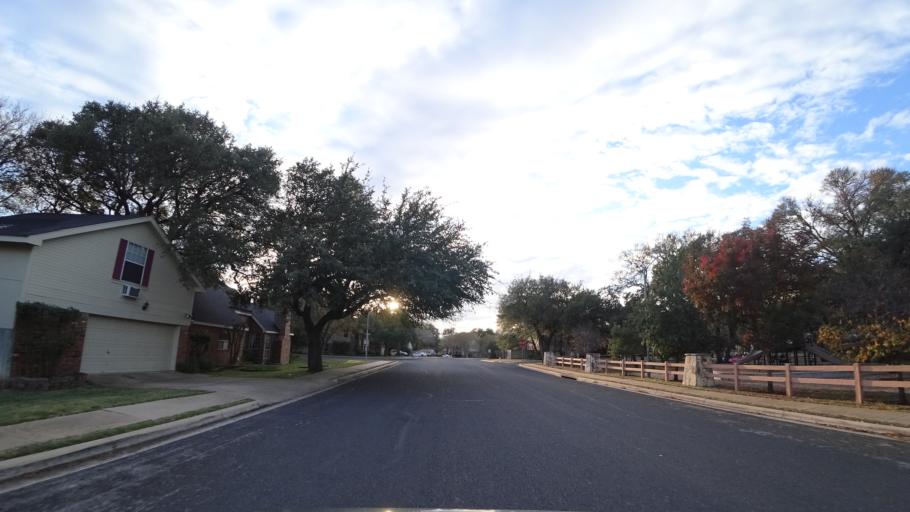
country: US
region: Texas
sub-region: Williamson County
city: Brushy Creek
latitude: 30.4903
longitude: -97.7377
